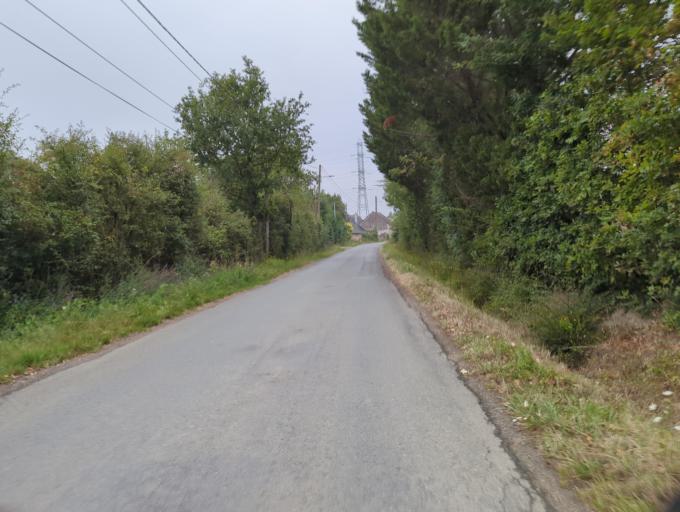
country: FR
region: Pays de la Loire
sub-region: Departement de Maine-et-Loire
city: Trelaze
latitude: 47.4806
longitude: -0.4776
